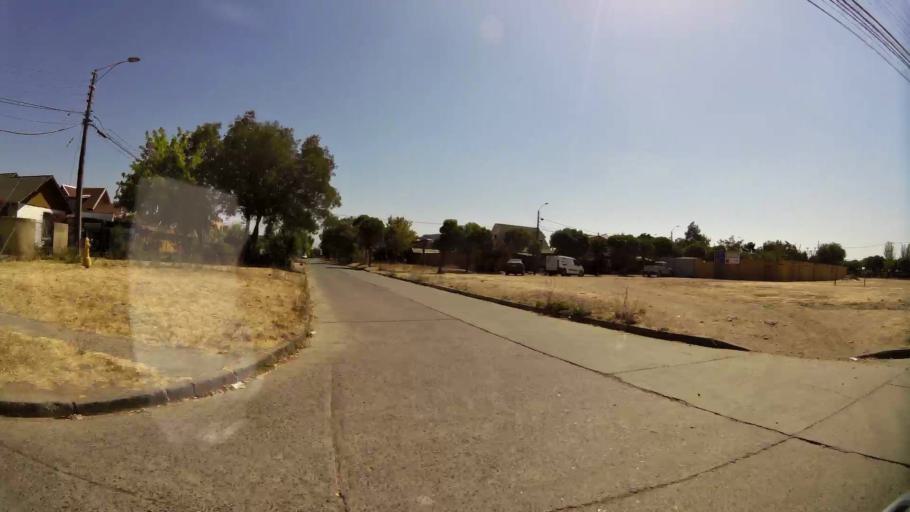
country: CL
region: Maule
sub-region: Provincia de Talca
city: Talca
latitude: -35.4157
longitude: -71.6463
